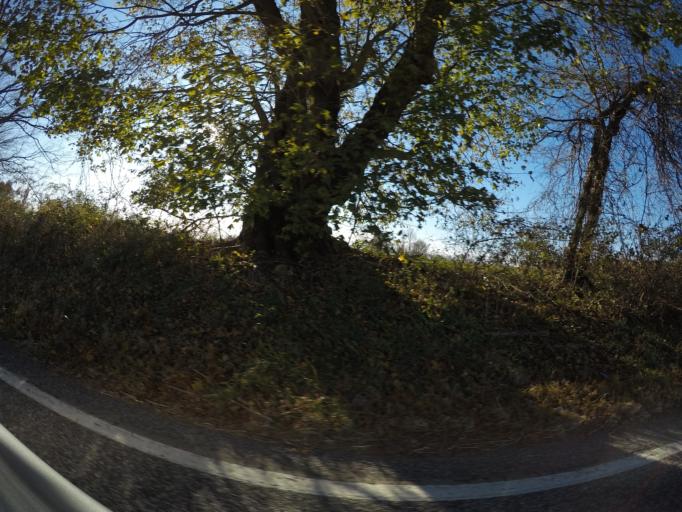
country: US
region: Maryland
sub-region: Harford County
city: Bel Air South
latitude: 39.5629
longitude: -76.2530
